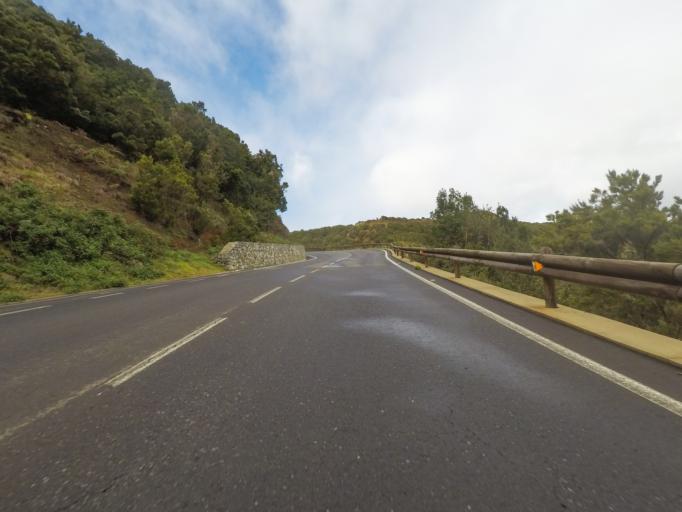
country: ES
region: Canary Islands
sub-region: Provincia de Santa Cruz de Tenerife
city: Vallehermosa
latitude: 28.1630
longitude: -17.2927
